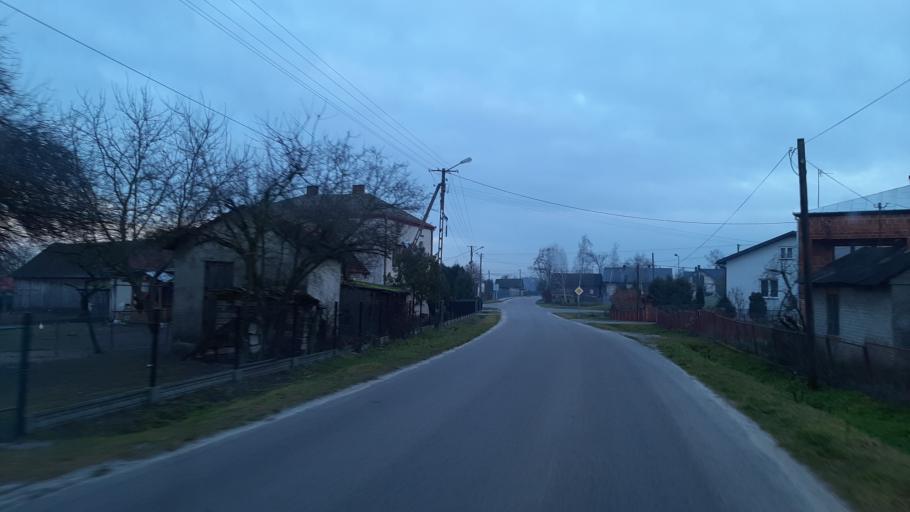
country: PL
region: Lublin Voivodeship
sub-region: Powiat lubartowski
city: Firlej
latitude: 51.5690
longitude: 22.5293
